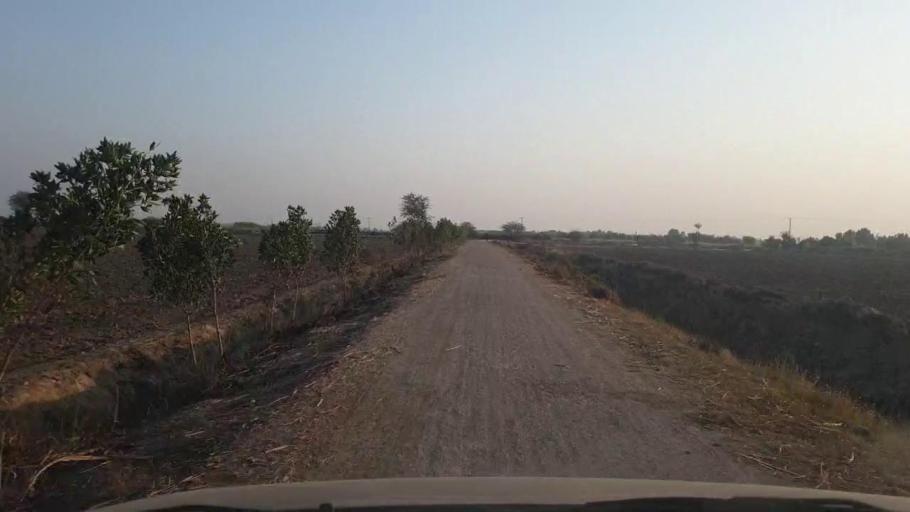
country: PK
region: Sindh
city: Mirwah Gorchani
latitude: 25.3474
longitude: 69.1533
